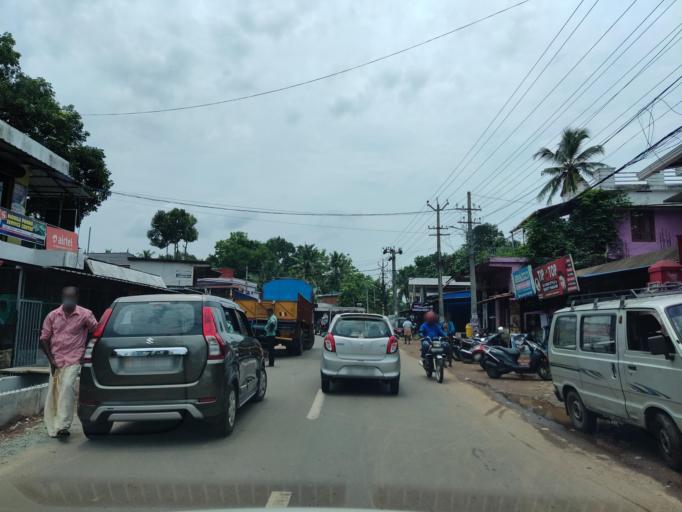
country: IN
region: Kerala
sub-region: Pattanamtitta
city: Adur
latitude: 9.2292
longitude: 76.6645
